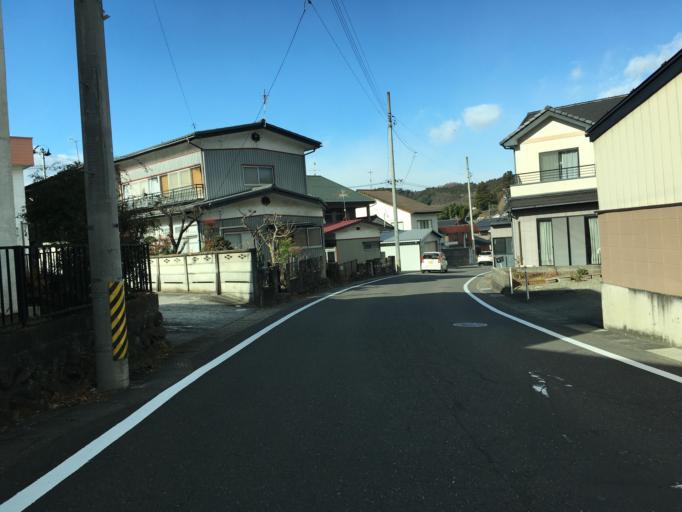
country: JP
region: Fukushima
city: Nihommatsu
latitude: 37.5981
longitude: 140.4495
